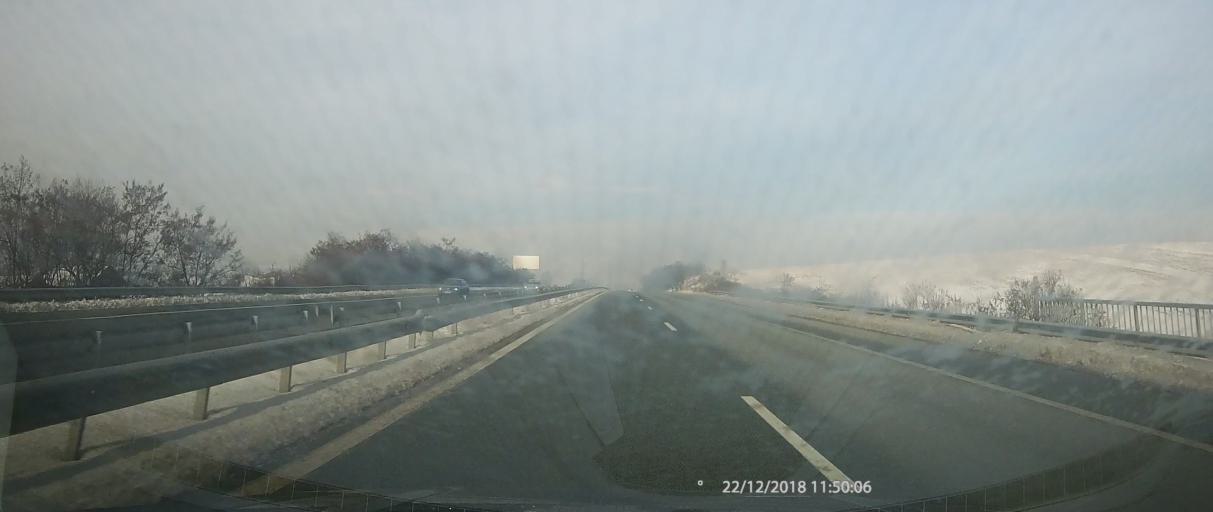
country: BG
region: Pernik
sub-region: Obshtina Pernik
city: Pernik
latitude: 42.5577
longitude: 23.1181
